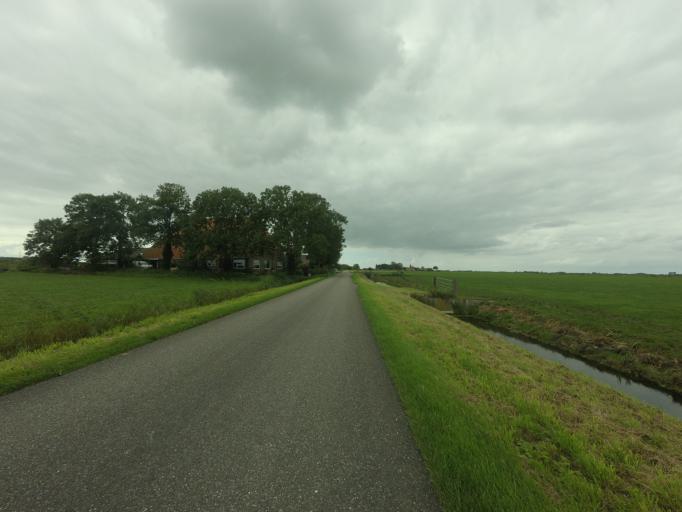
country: NL
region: Friesland
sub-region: Sudwest Fryslan
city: Bolsward
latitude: 52.9862
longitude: 5.5309
